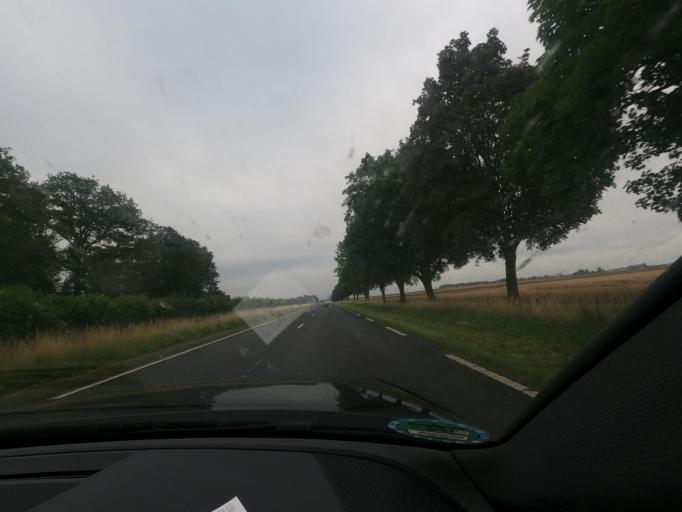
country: FR
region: Picardie
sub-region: Departement de la Somme
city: Rosieres-en-Santerre
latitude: 49.7649
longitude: 2.6299
